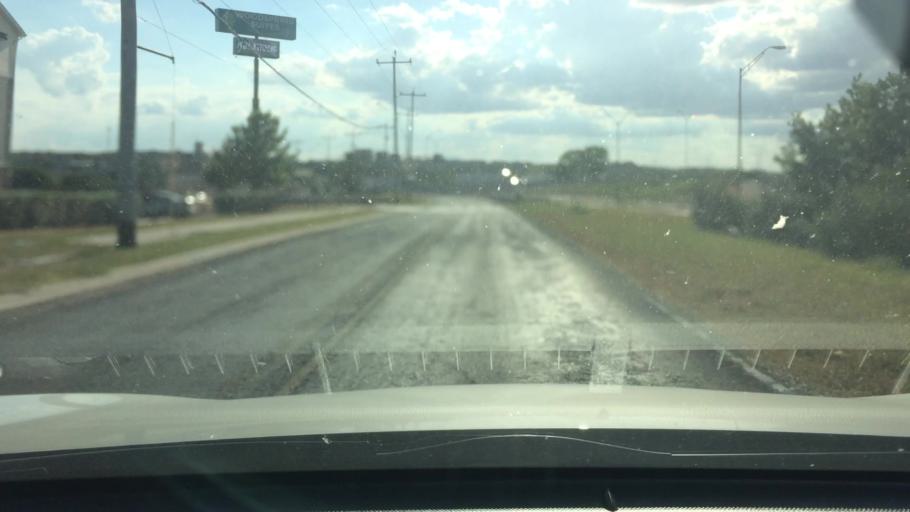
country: US
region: Texas
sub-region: Bexar County
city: Live Oak
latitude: 29.5630
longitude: -98.3367
